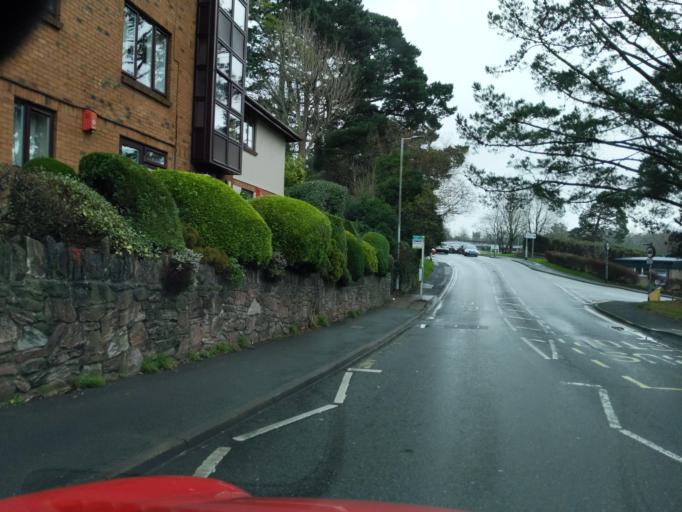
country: GB
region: England
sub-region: Devon
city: Plympton
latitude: 50.3873
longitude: -4.0534
